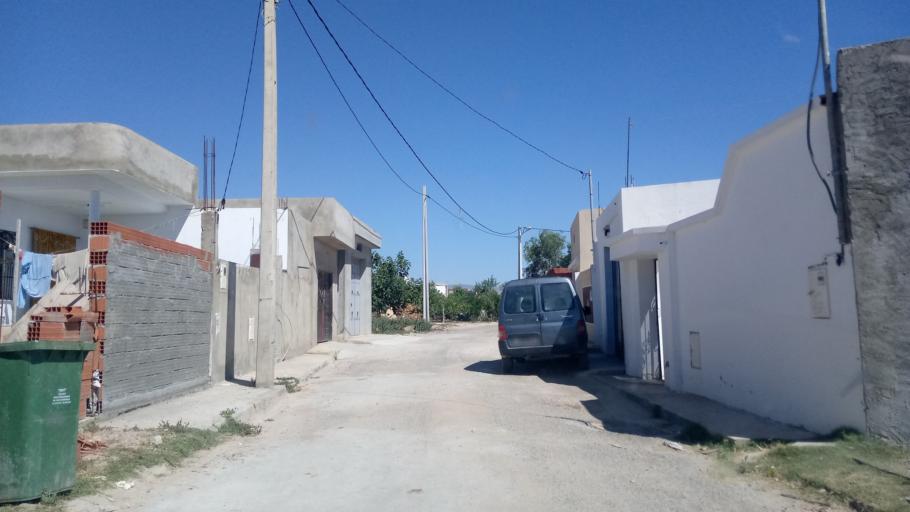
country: TN
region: Al Qayrawan
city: Sbikha
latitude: 36.1294
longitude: 10.0901
